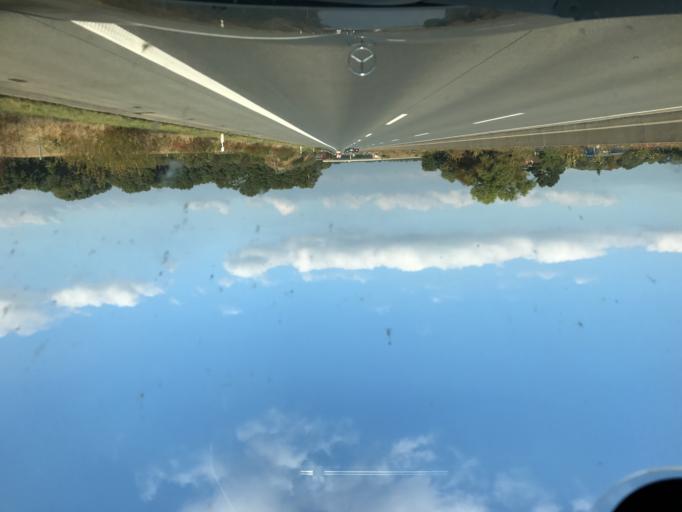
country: DE
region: Lower Saxony
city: Gross Meckelsen
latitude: 53.2783
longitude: 9.4682
